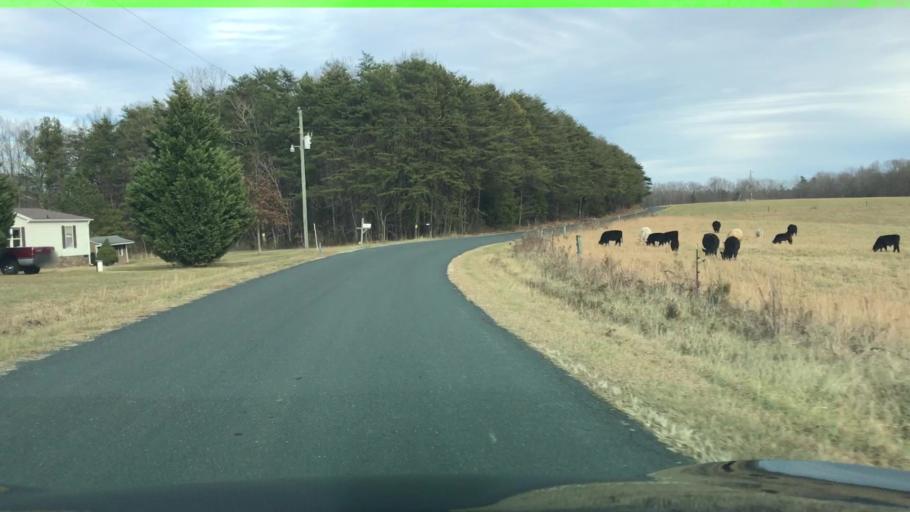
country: US
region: Virginia
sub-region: Campbell County
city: Concord
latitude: 37.2466
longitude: -78.8994
